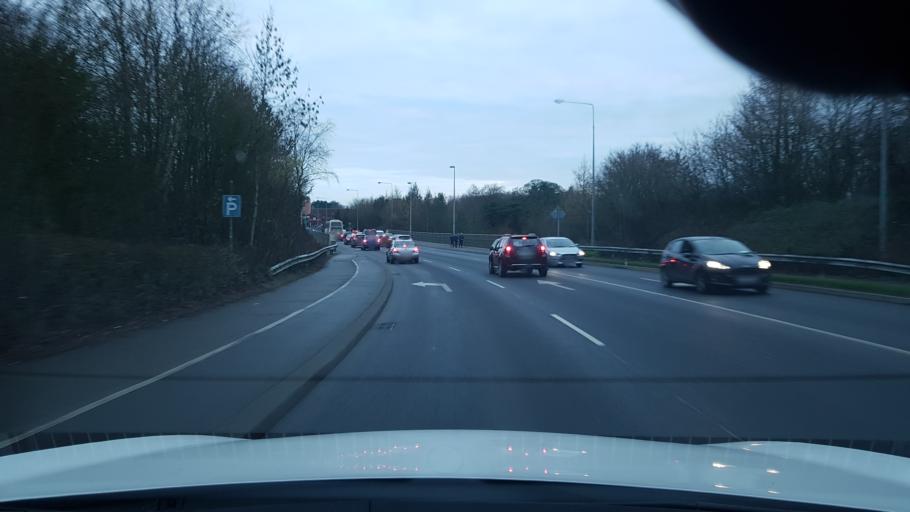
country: IE
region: Leinster
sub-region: An Mhi
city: Navan
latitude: 53.6577
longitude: -6.6862
